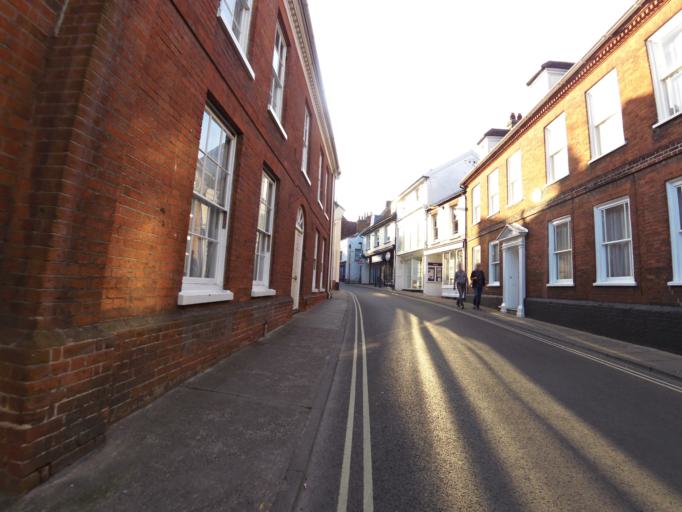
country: GB
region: England
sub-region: Suffolk
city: Woodbridge
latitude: 52.0929
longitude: 1.3157
